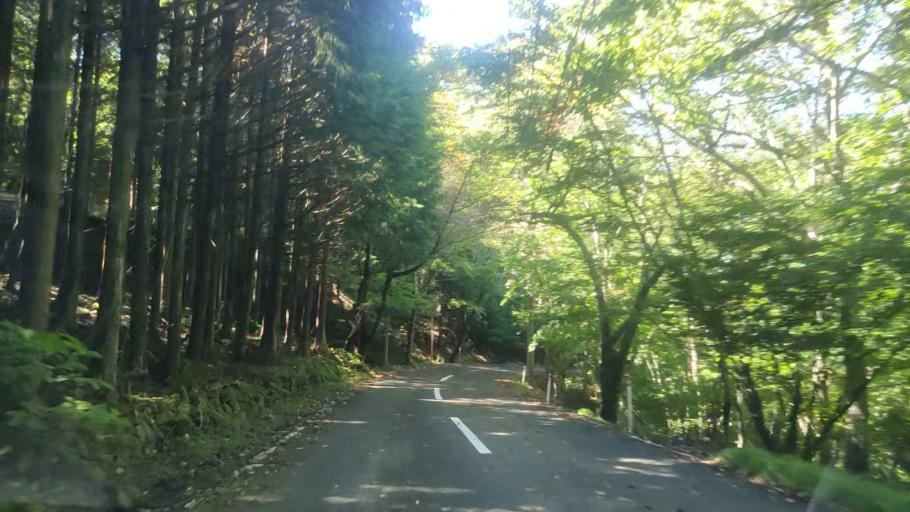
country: JP
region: Yamanashi
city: Fujikawaguchiko
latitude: 35.5718
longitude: 138.7736
